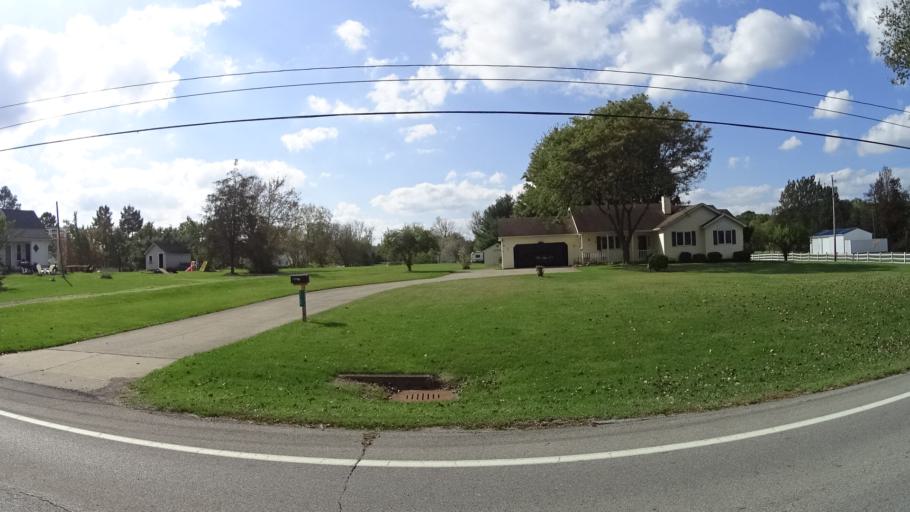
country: US
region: Ohio
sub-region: Lorain County
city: Grafton
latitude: 41.2660
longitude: -82.0496
